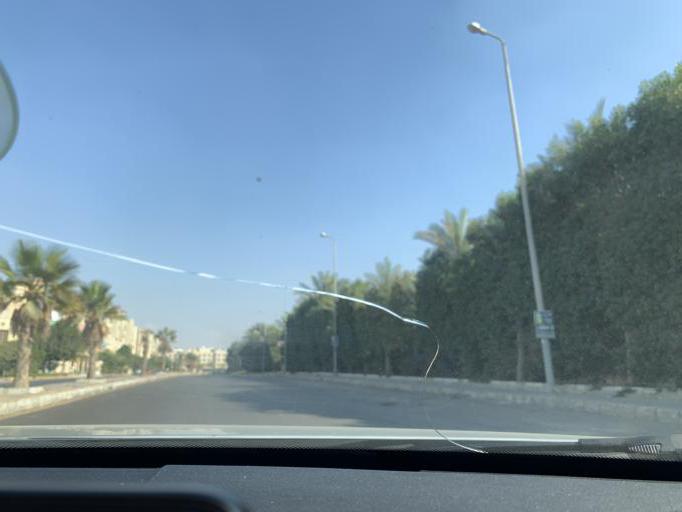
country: EG
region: Muhafazat al Qalyubiyah
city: Al Khankah
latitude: 30.0187
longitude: 31.4818
